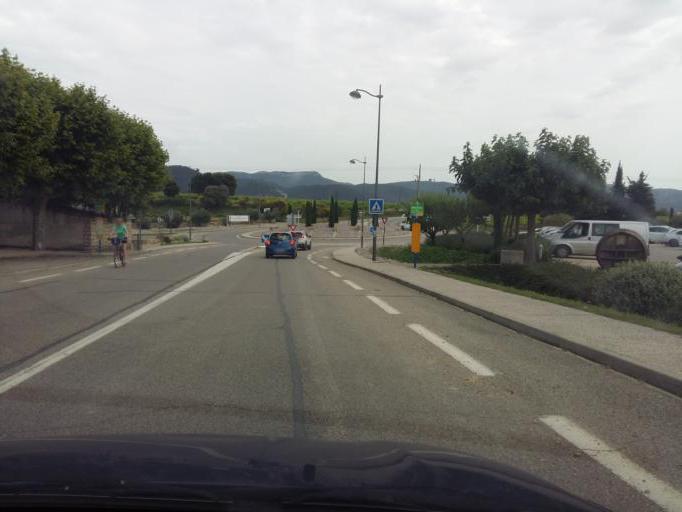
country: FR
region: Provence-Alpes-Cote d'Azur
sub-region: Departement du Vaucluse
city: Sablet
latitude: 44.2254
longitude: 4.9882
